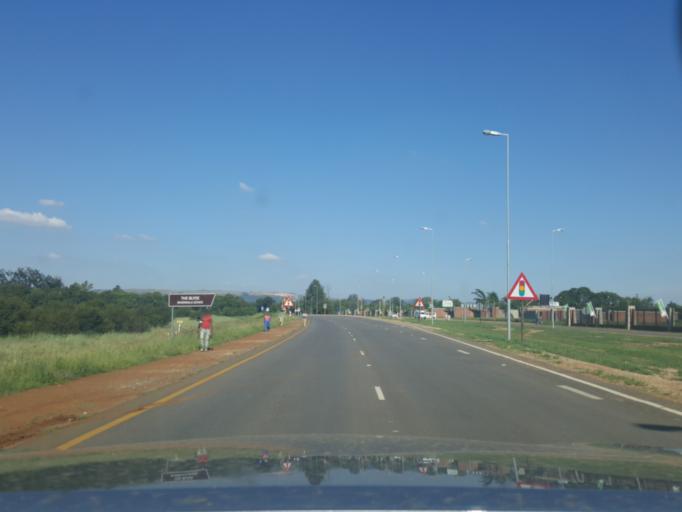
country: ZA
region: Gauteng
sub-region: City of Tshwane Metropolitan Municipality
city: Cullinan
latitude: -25.7539
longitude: 28.3757
